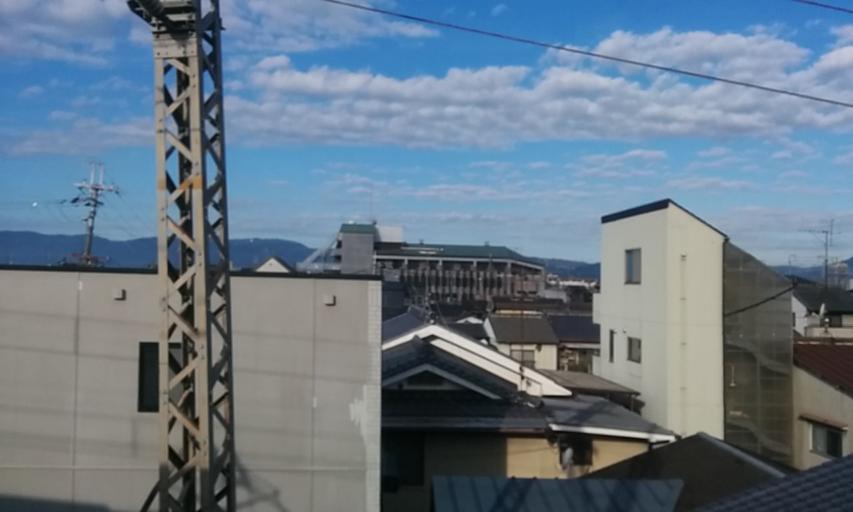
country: JP
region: Kyoto
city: Kyoto
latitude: 34.9834
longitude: 135.7528
